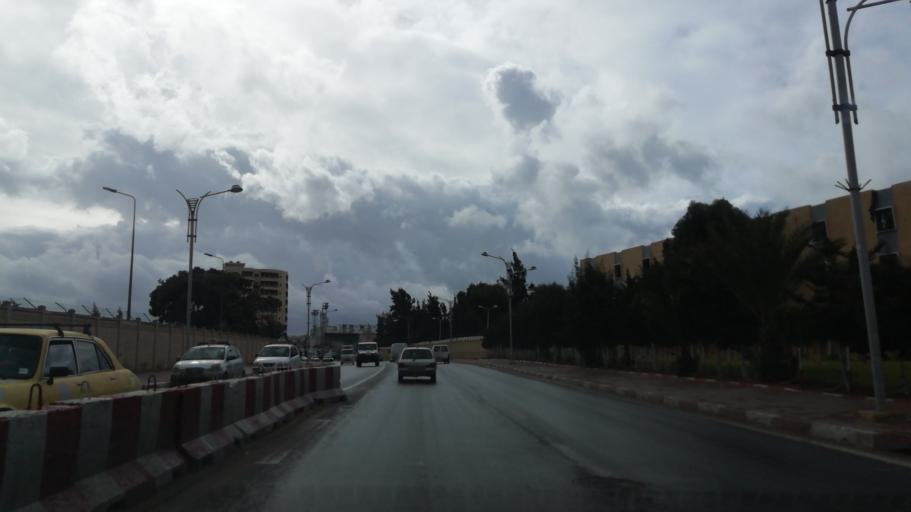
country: DZ
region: Oran
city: Oran
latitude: 35.6818
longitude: -0.6724
